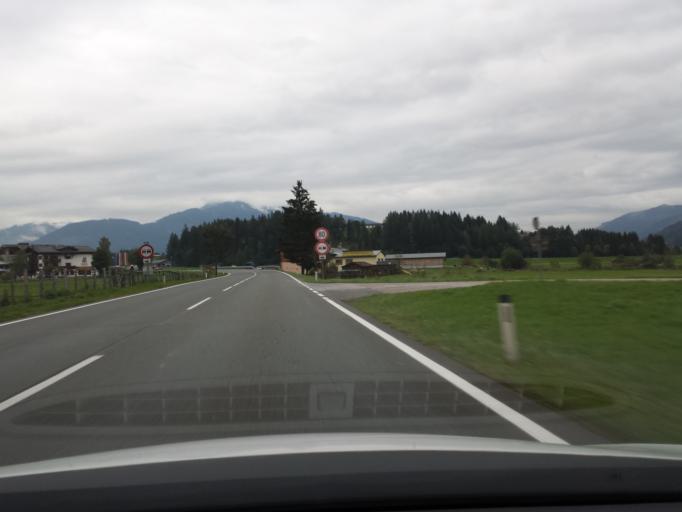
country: AT
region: Salzburg
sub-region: Politischer Bezirk Zell am See
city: Saalfelden am Steinernen Meer
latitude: 47.4569
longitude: 12.8299
